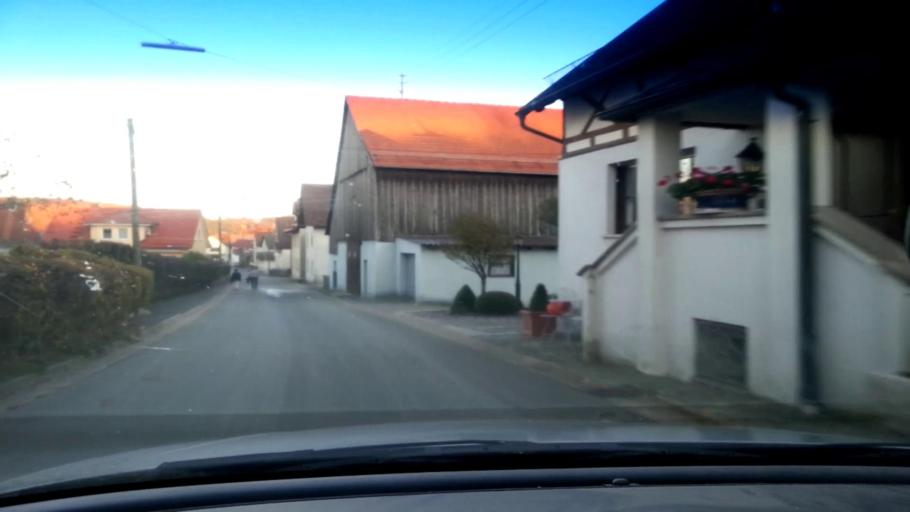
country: DE
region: Bavaria
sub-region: Upper Franconia
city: Heiligenstadt
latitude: 49.8564
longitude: 11.1147
